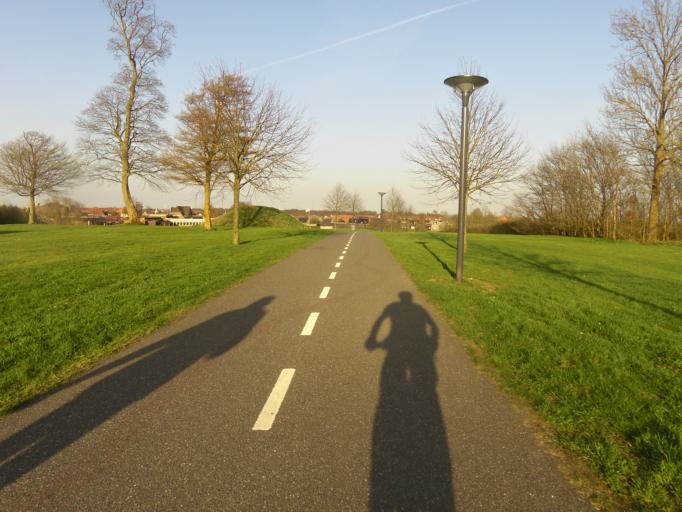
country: DK
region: South Denmark
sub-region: Vejen Kommune
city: Vejen
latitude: 55.4734
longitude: 9.1291
